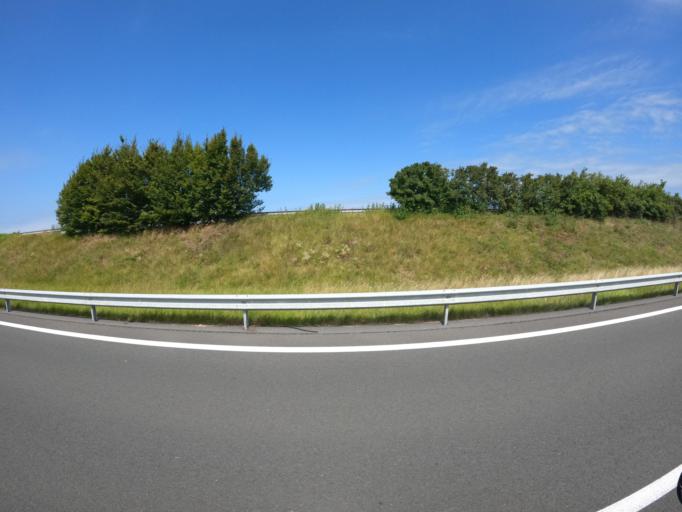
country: FR
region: Poitou-Charentes
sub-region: Departement des Deux-Sevres
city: Mauze-sur-le-Mignon
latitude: 46.2182
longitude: -0.6116
